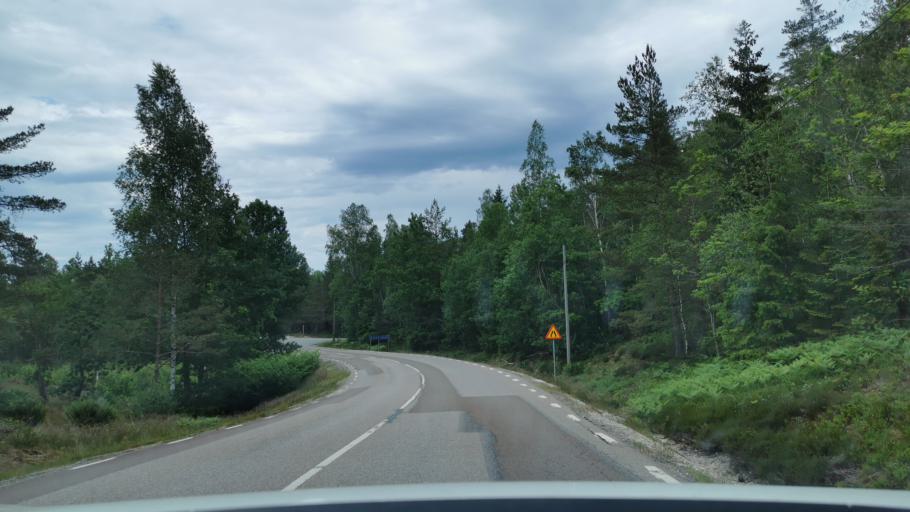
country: SE
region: Vaestra Goetaland
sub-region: Melleruds Kommun
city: Mellerud
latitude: 58.8329
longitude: 12.4121
